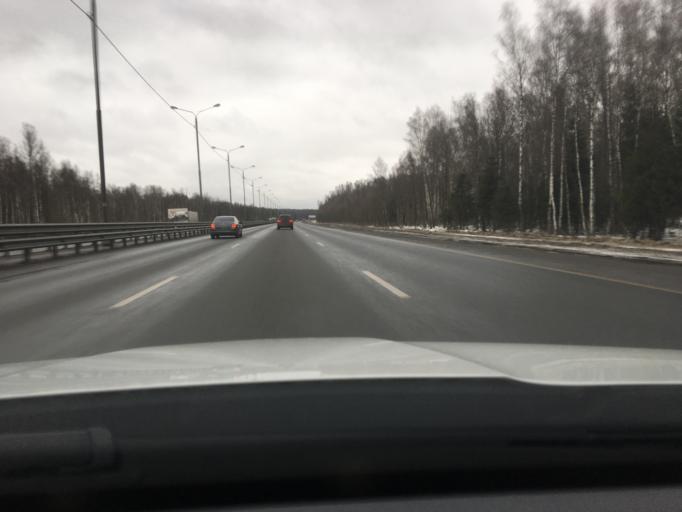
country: RU
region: Moskovskaya
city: Novyy Byt
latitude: 55.1155
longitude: 37.5769
